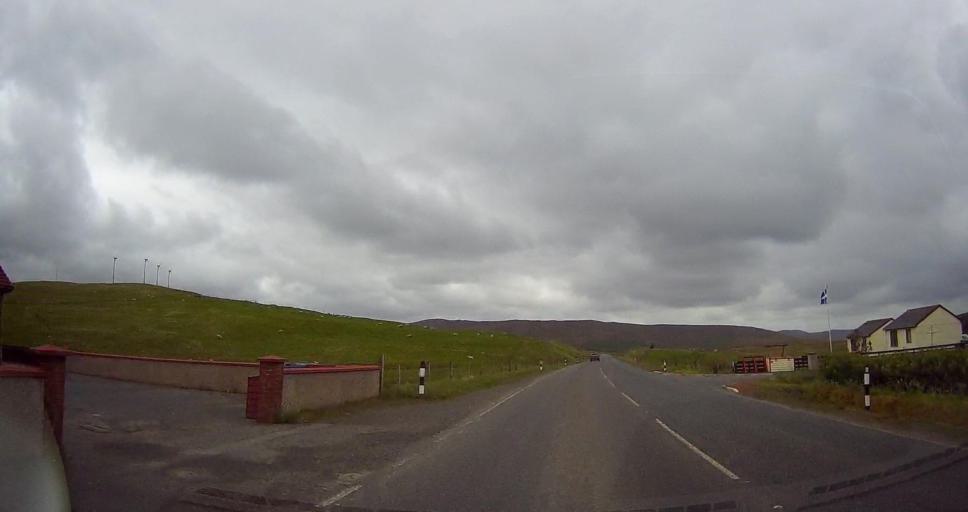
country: GB
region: Scotland
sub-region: Shetland Islands
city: Lerwick
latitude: 60.3785
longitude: -1.3406
